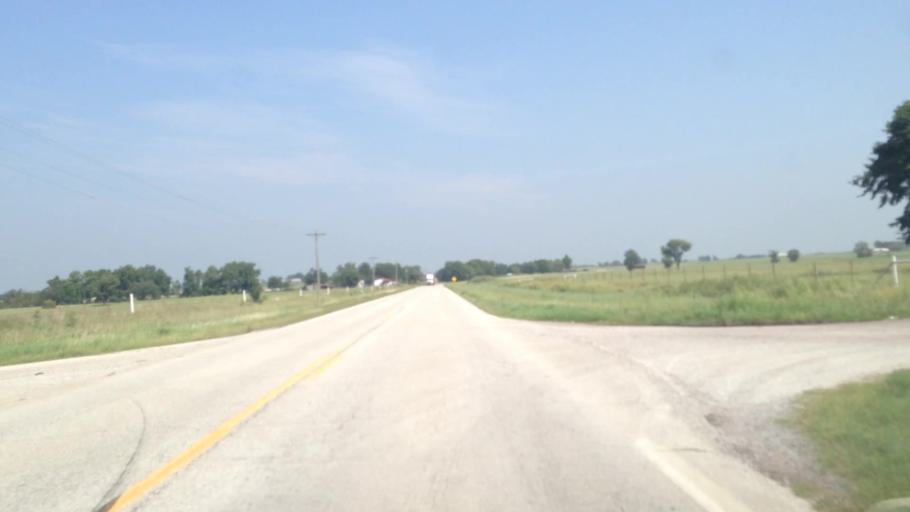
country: US
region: Oklahoma
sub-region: Craig County
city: Vinita
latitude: 36.8154
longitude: -95.1436
